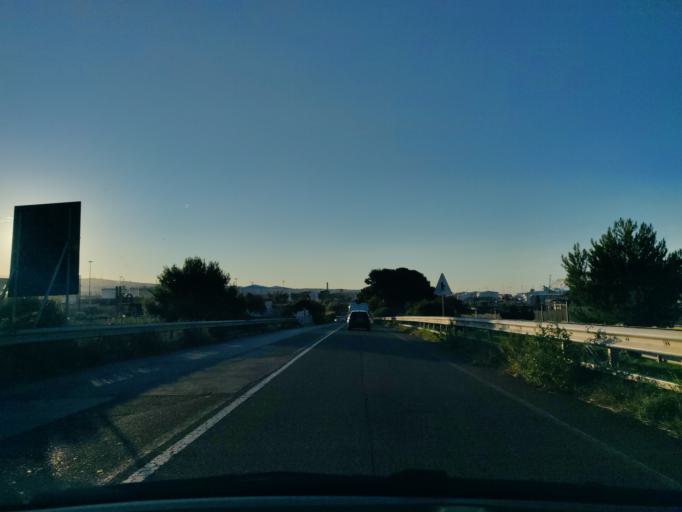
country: IT
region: Latium
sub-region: Citta metropolitana di Roma Capitale
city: Aurelia
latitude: 42.1144
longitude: 11.7735
